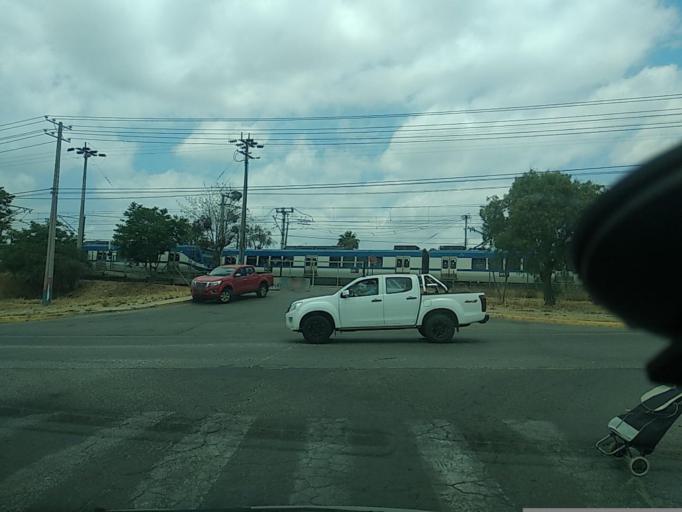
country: CL
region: Valparaiso
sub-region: Provincia de Marga Marga
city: Villa Alemana
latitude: -33.0424
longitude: -71.4076
